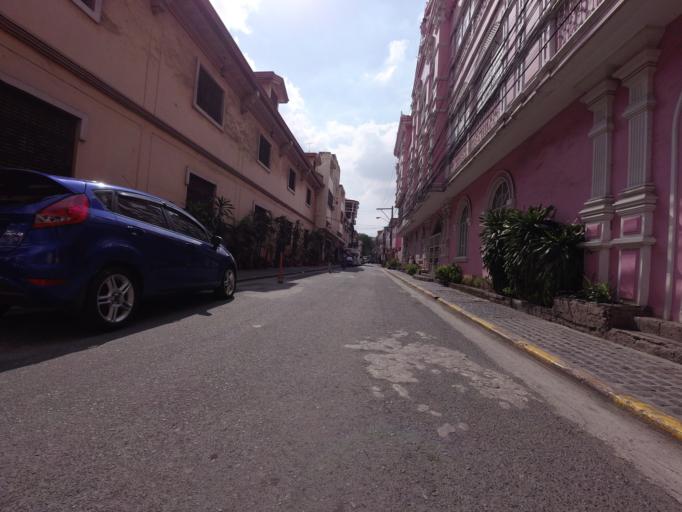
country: PH
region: Metro Manila
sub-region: City of Manila
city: Quiapo
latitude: 14.5925
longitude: 120.9752
